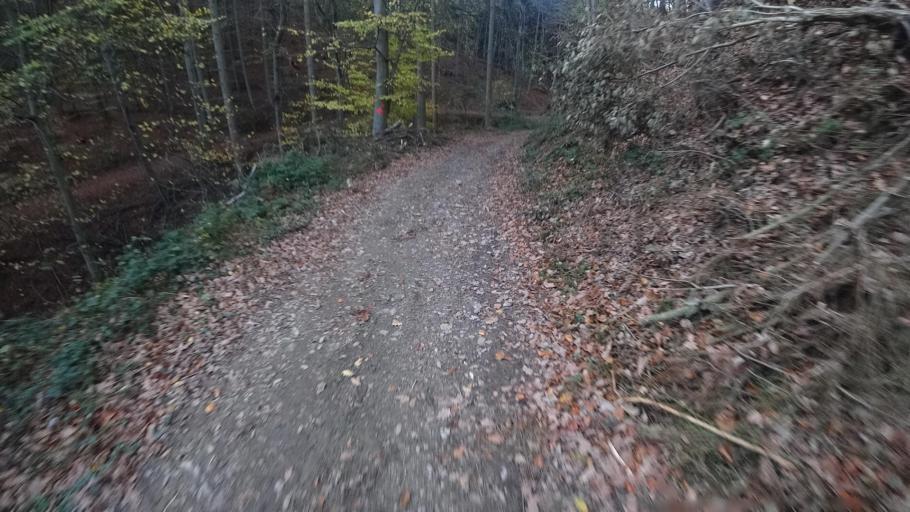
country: DE
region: Rheinland-Pfalz
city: Lind
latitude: 50.5217
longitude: 6.9437
